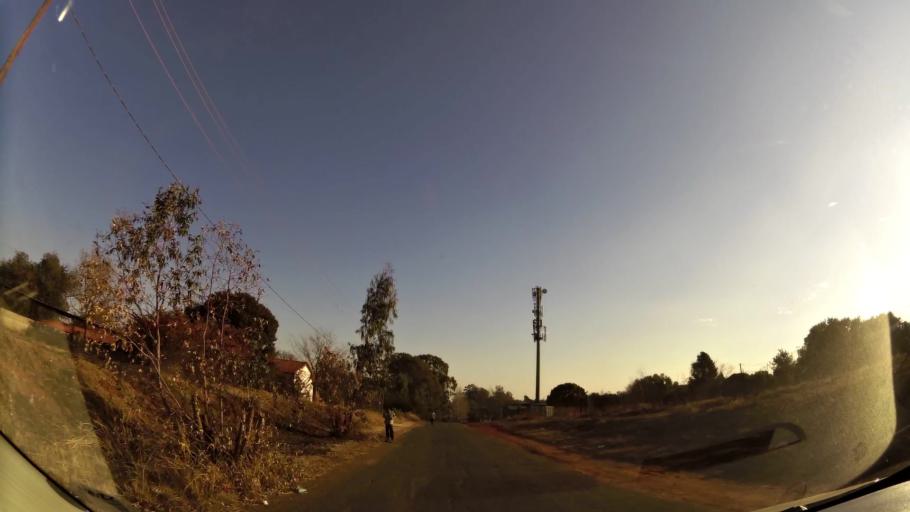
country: ZA
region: Gauteng
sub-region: West Rand District Municipality
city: Randfontein
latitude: -26.2179
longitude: 27.6513
